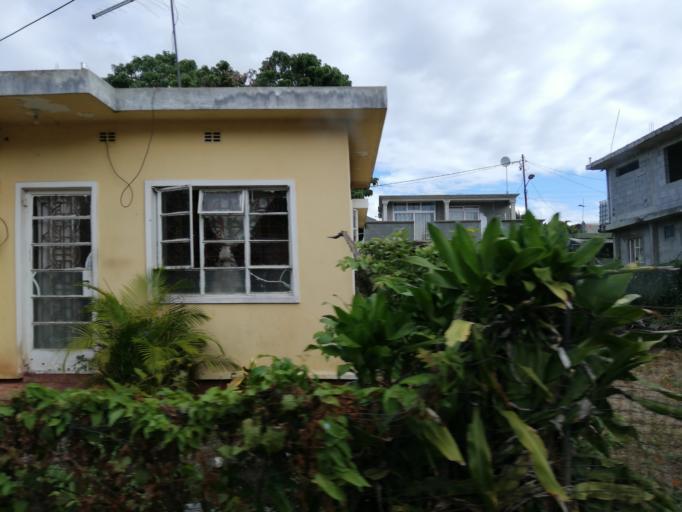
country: MU
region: Black River
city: Gros Cailloux
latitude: -20.2301
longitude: 57.4524
